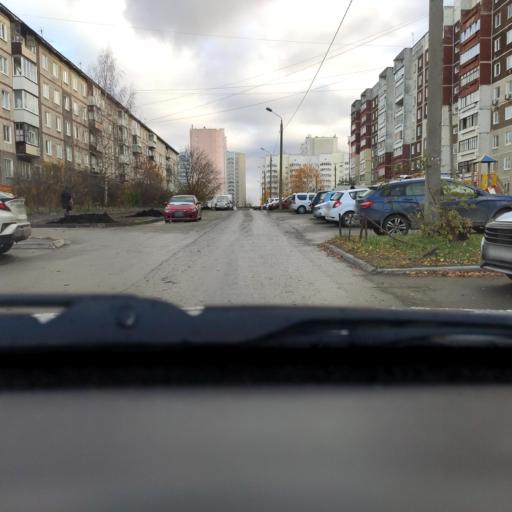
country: RU
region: Perm
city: Kondratovo
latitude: 58.0364
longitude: 56.1354
